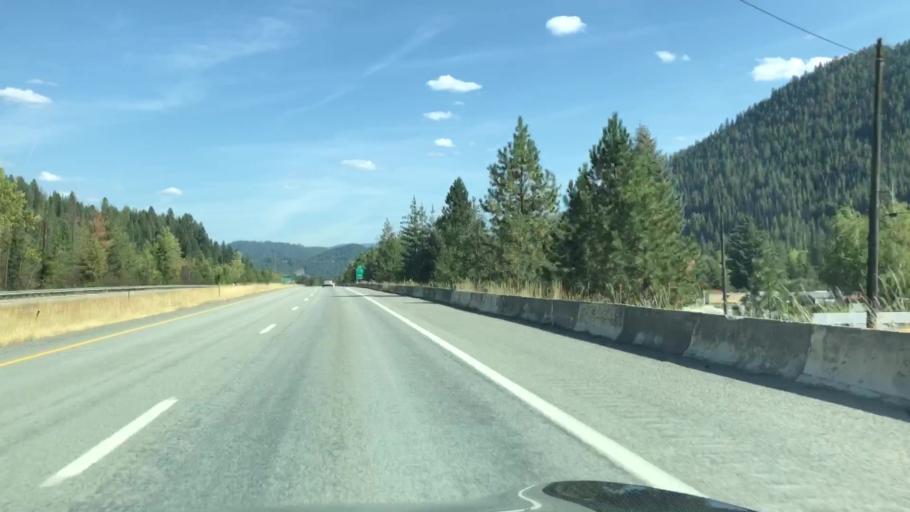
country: US
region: Idaho
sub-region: Shoshone County
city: Osburn
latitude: 47.5137
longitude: -116.0282
